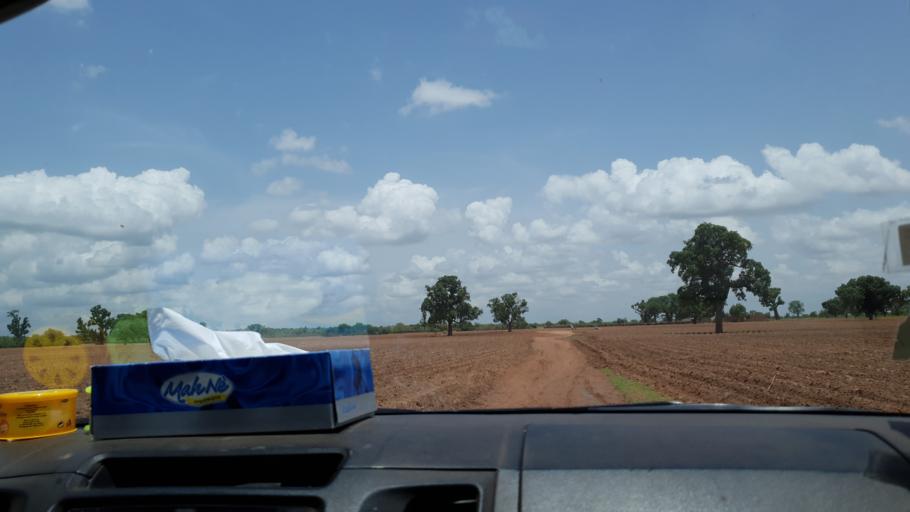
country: ML
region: Koulikoro
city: Banamba
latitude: 13.3795
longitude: -7.2012
